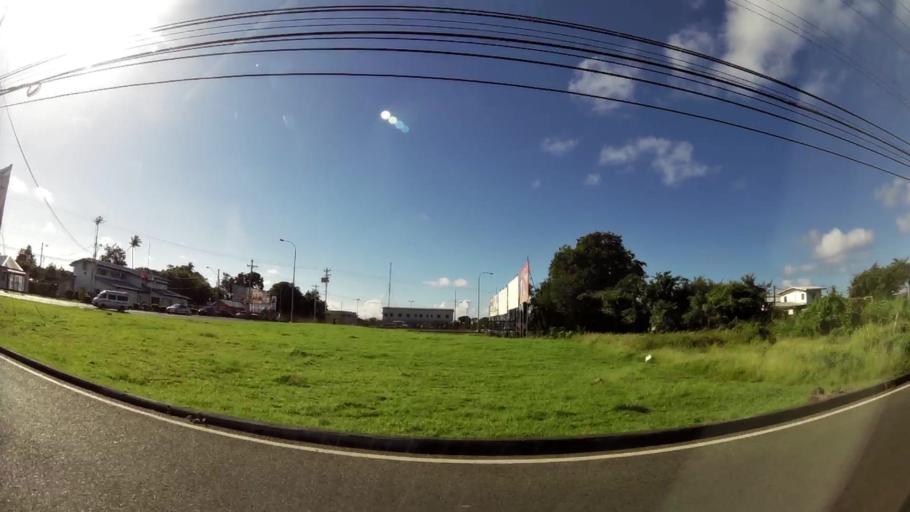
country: TT
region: Tobago
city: Scarborough
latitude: 11.1538
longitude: -60.8384
